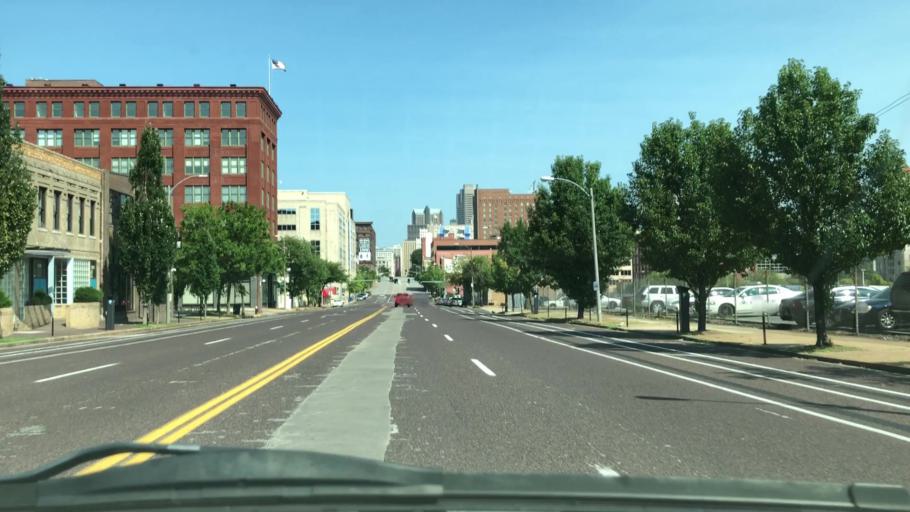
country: US
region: Missouri
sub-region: City of Saint Louis
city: St. Louis
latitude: 38.6324
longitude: -90.2109
